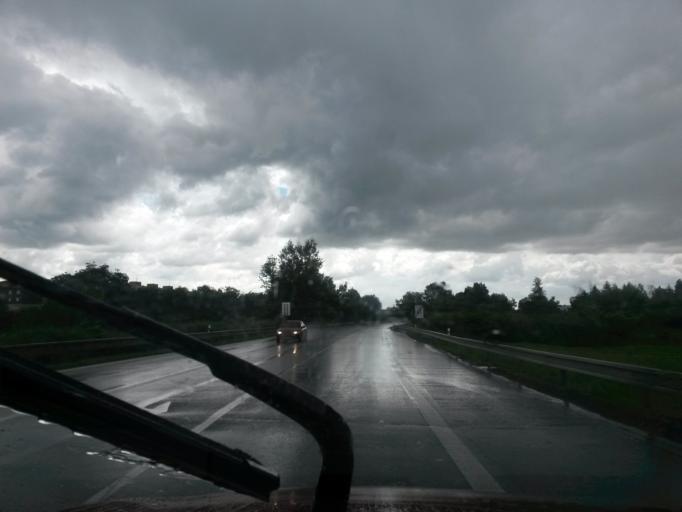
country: SK
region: Presovsky
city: Vranov nad Topl'ou
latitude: 48.8828
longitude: 21.6854
